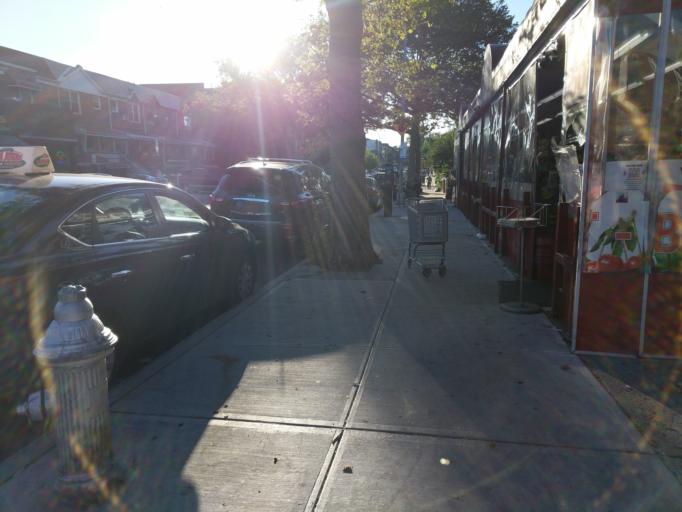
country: US
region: New York
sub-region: Queens County
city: Long Island City
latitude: 40.7603
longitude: -73.9071
